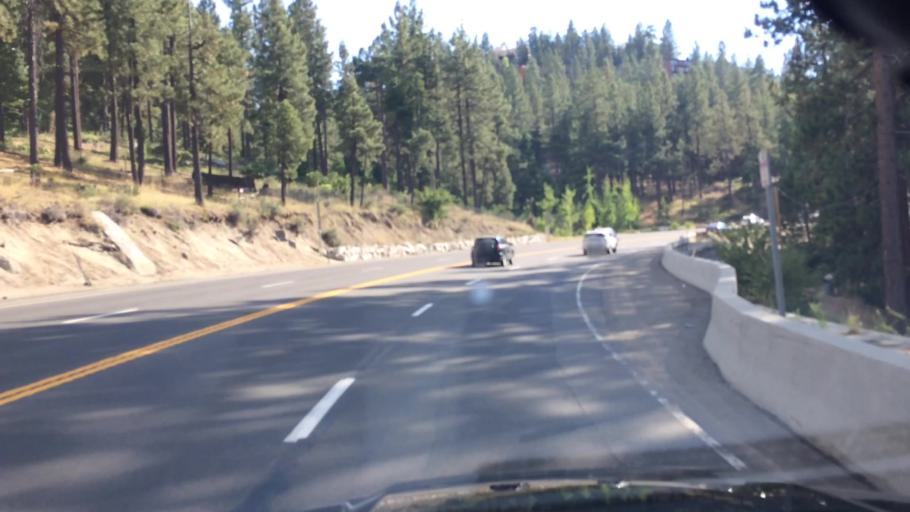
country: US
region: Nevada
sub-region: Douglas County
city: Kingsbury
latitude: 39.0029
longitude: -119.9484
